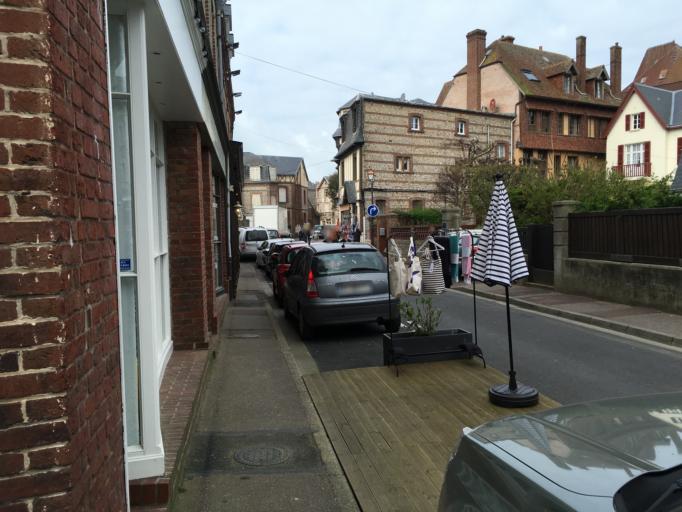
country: FR
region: Haute-Normandie
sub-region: Departement de la Seine-Maritime
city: Etretat
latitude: 49.7081
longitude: 0.2045
